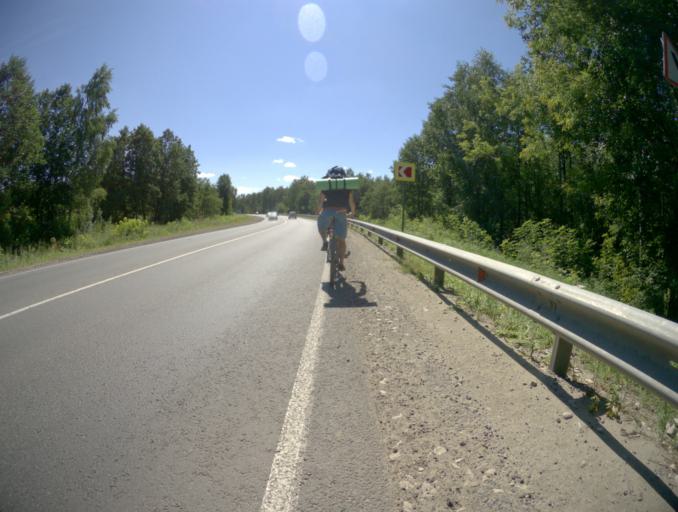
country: RU
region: Nizjnij Novgorod
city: Neklyudovo
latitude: 56.4298
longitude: 43.9899
